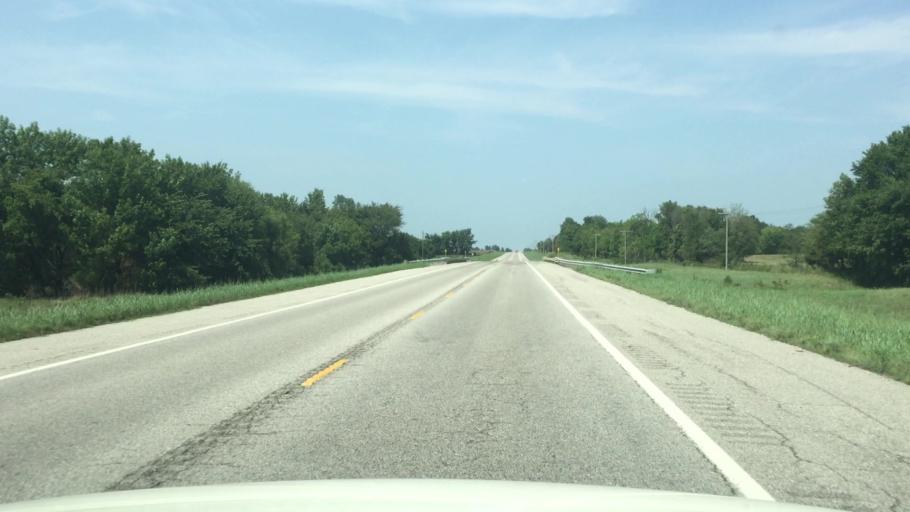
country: US
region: Kansas
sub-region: Crawford County
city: Pittsburg
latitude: 37.2543
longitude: -94.7051
